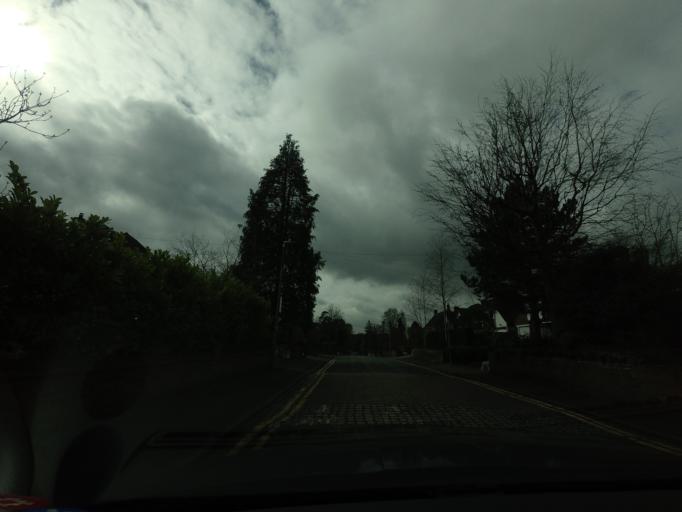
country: GB
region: England
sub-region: Kent
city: Sevenoaks
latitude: 51.2832
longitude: 0.1851
